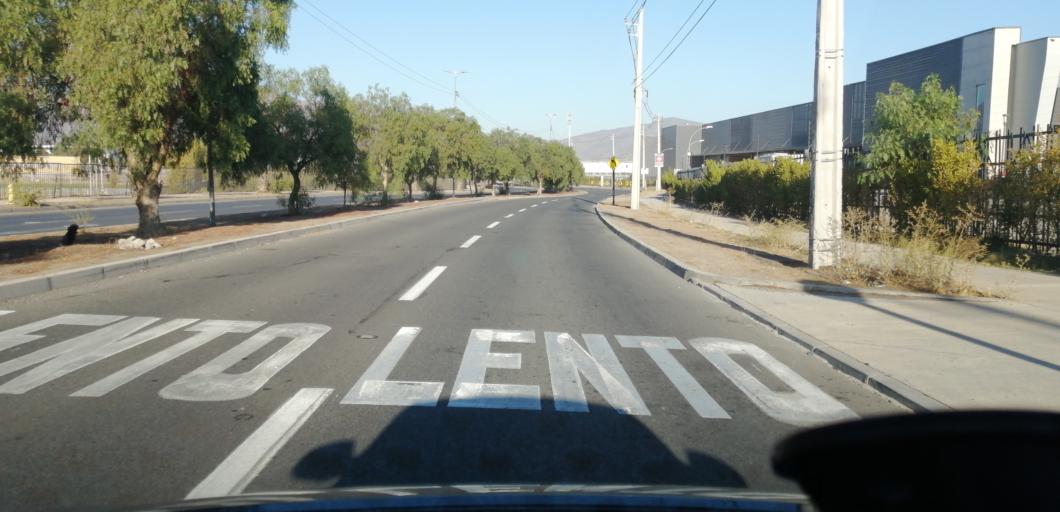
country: CL
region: Santiago Metropolitan
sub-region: Provincia de Santiago
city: Lo Prado
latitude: -33.4491
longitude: -70.8478
